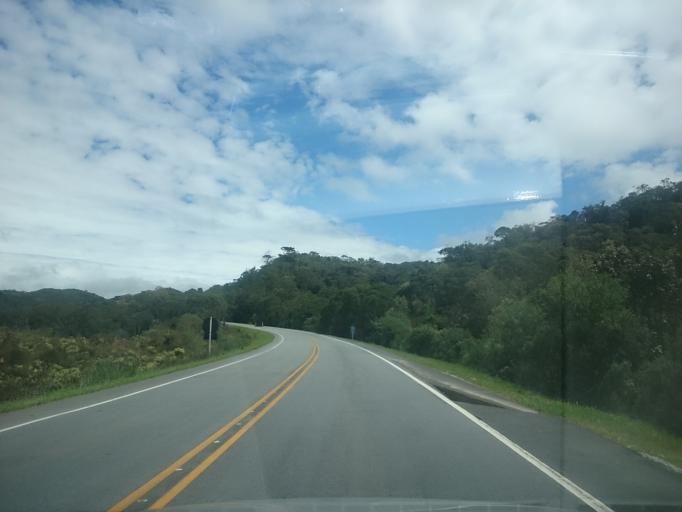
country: BR
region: Santa Catarina
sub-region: Anitapolis
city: Anitapolis
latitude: -27.6882
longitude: -49.0374
